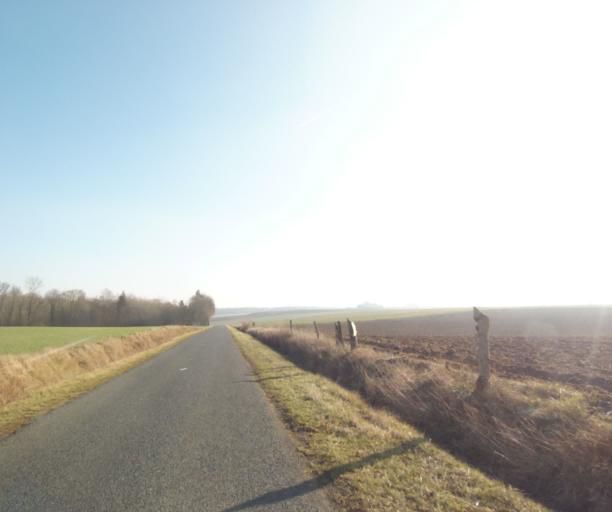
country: FR
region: Champagne-Ardenne
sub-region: Departement de la Haute-Marne
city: Chevillon
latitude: 48.4866
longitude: 5.0826
